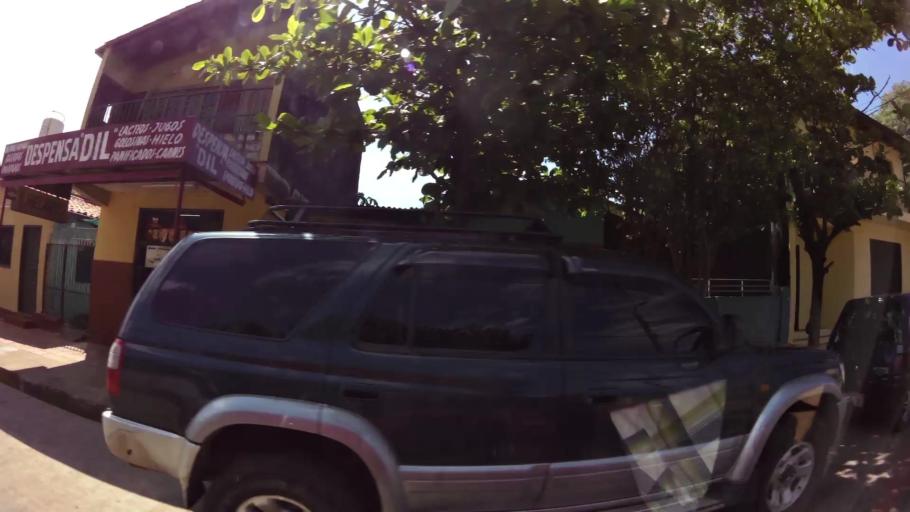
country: PY
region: Central
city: San Lorenzo
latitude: -25.2685
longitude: -57.4953
